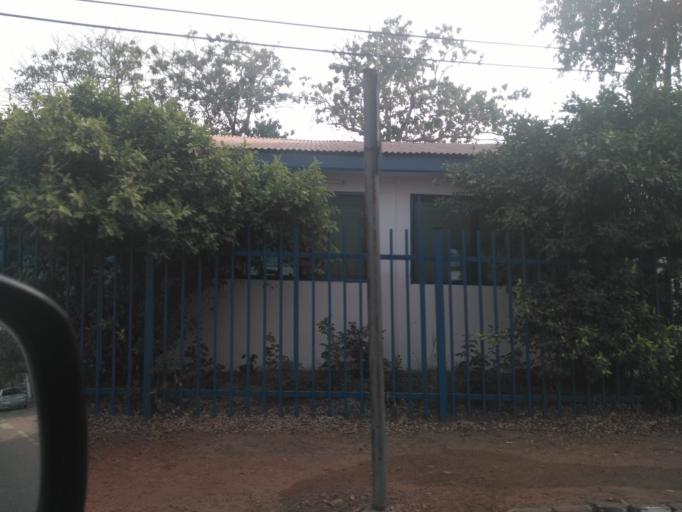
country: GH
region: Greater Accra
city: Accra
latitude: 5.6024
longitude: -0.1937
